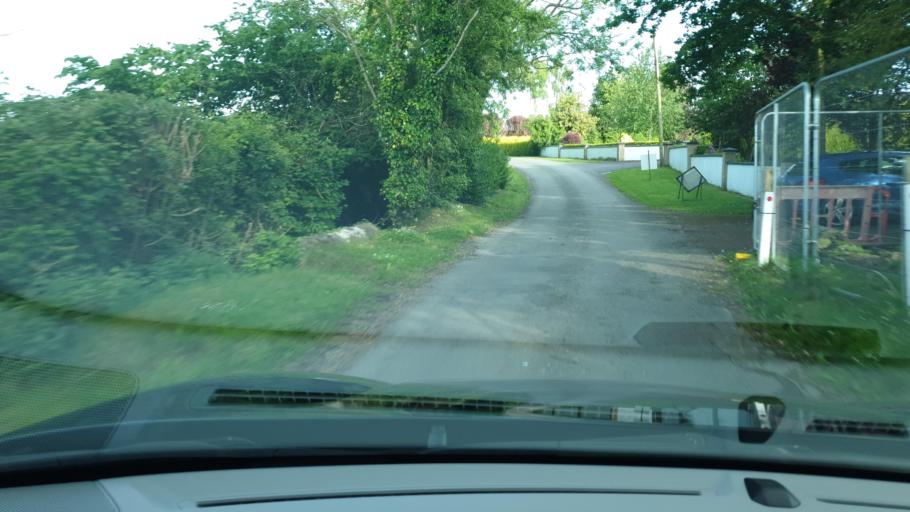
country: IE
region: Leinster
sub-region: An Mhi
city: Ratoath
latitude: 53.5585
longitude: -6.4351
